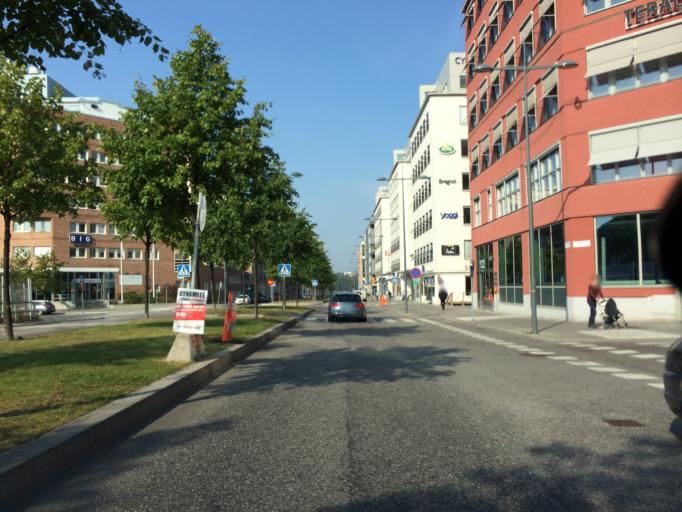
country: SE
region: Stockholm
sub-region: Solna Kommun
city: Solna
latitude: 59.3374
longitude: 18.0087
